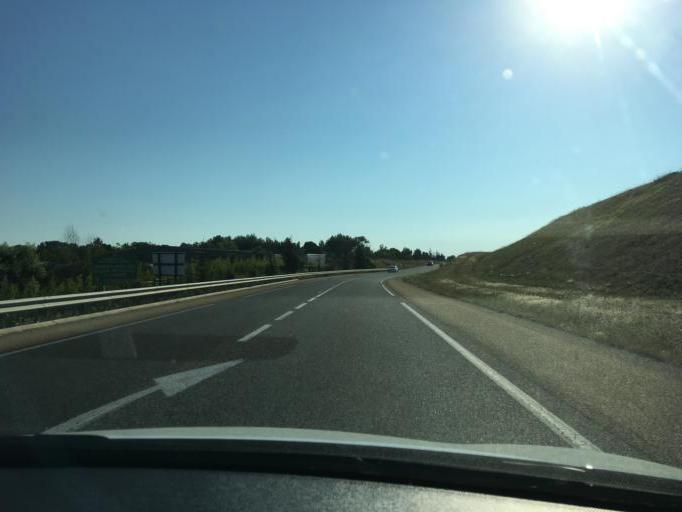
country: FR
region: Provence-Alpes-Cote d'Azur
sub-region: Departement des Bouches-du-Rhone
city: Charleval
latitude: 43.7185
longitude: 5.2609
